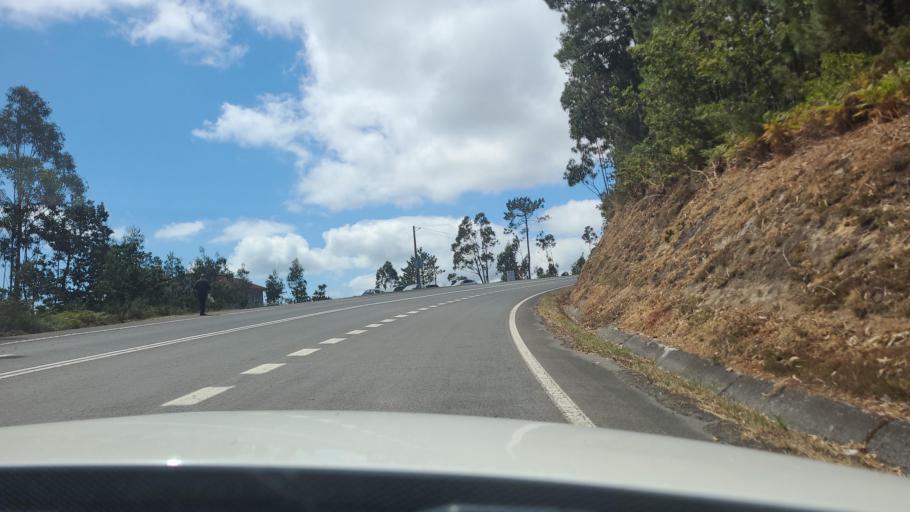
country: ES
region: Galicia
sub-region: Provincia da Coruna
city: Corcubion
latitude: 42.9105
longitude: -9.1415
